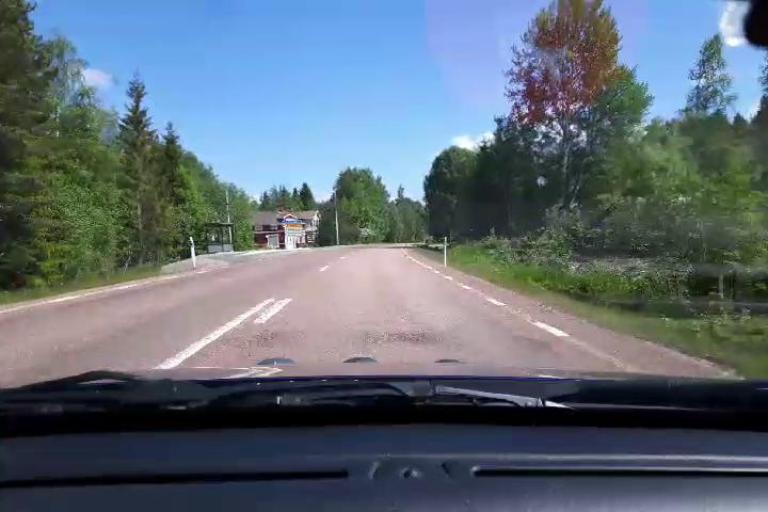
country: SE
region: Gaevleborg
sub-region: Hudiksvalls Kommun
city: Delsbo
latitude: 61.8044
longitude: 16.4650
